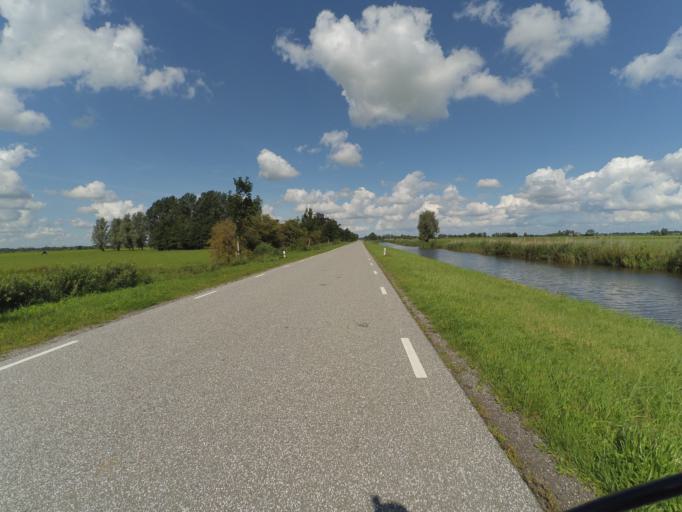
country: NL
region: Friesland
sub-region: Gemeente Achtkarspelen
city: Augustinusga
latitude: 53.2504
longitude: 6.1849
